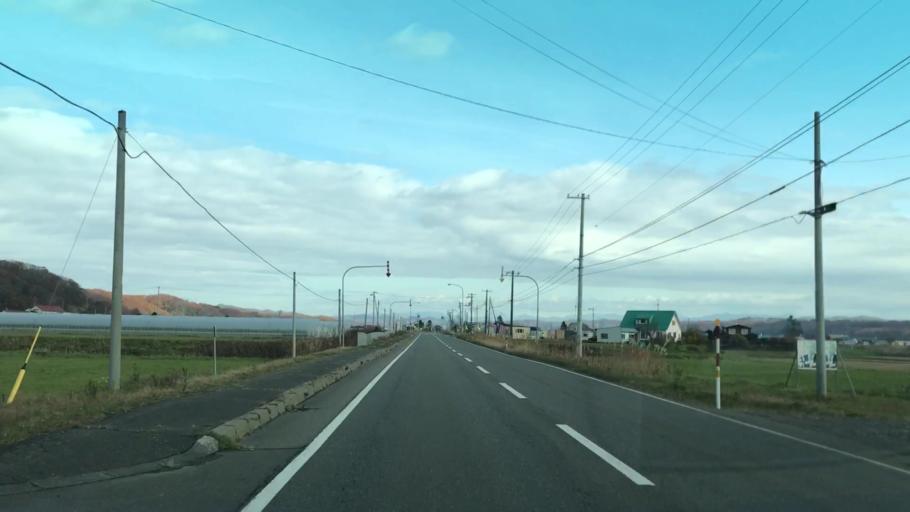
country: JP
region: Hokkaido
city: Shizunai-furukawacho
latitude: 42.5450
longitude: 142.0608
